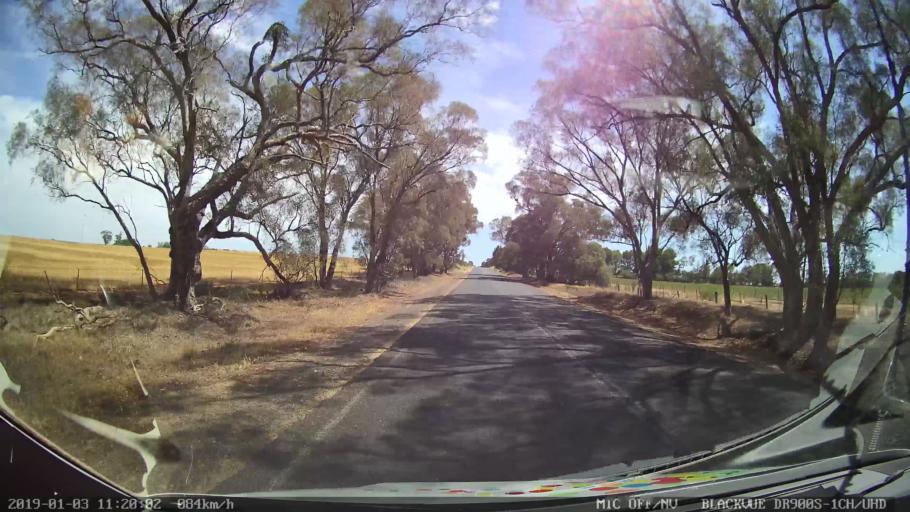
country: AU
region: New South Wales
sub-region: Young
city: Young
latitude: -34.1061
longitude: 148.2553
